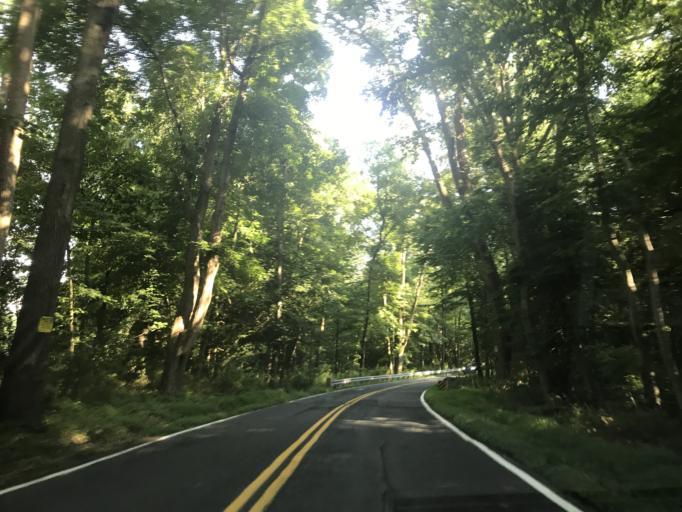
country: US
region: Maryland
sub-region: Harford County
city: Aberdeen
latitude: 39.5150
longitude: -76.1239
